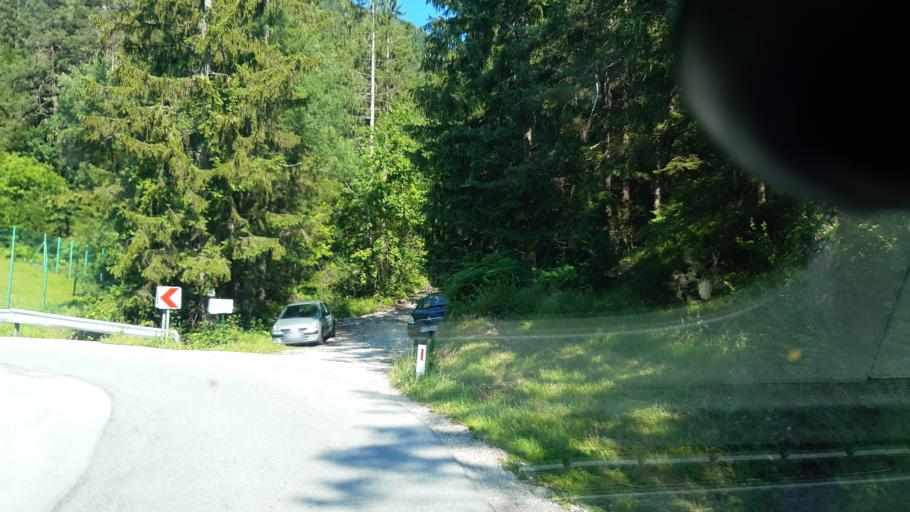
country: SI
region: Trzic
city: Bistrica pri Trzicu
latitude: 46.3623
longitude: 14.2843
